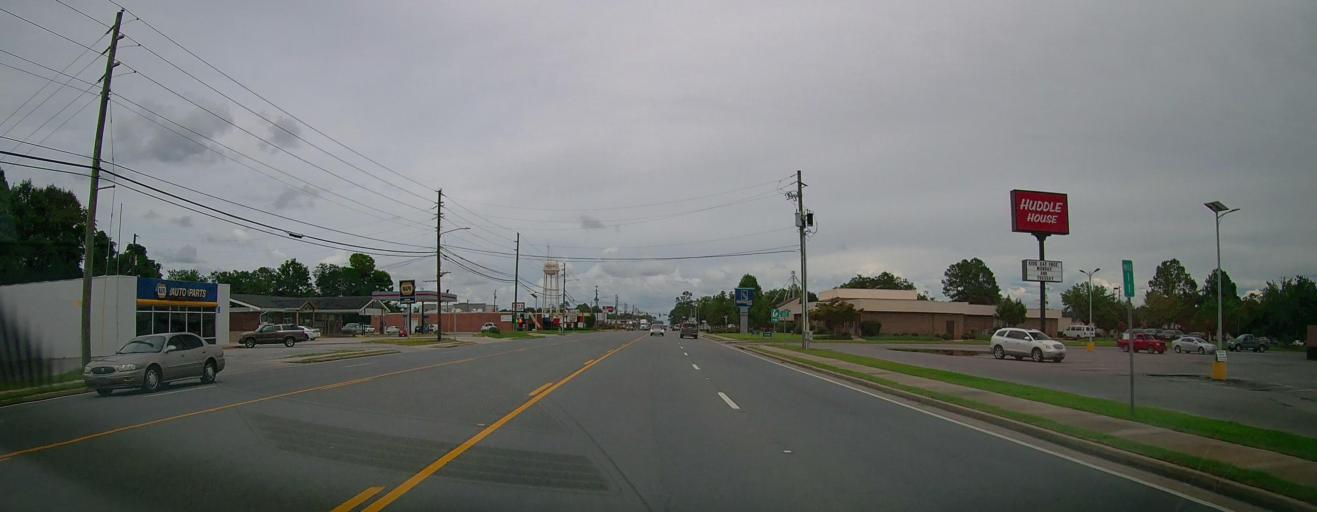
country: US
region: Georgia
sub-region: Appling County
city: Baxley
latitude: 31.7781
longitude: -82.3468
